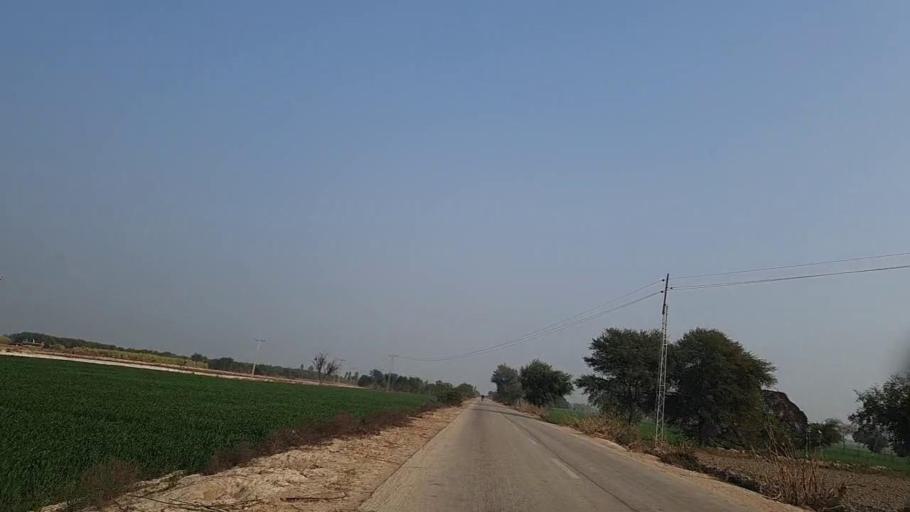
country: PK
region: Sindh
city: Sann
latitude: 26.1402
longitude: 68.1612
